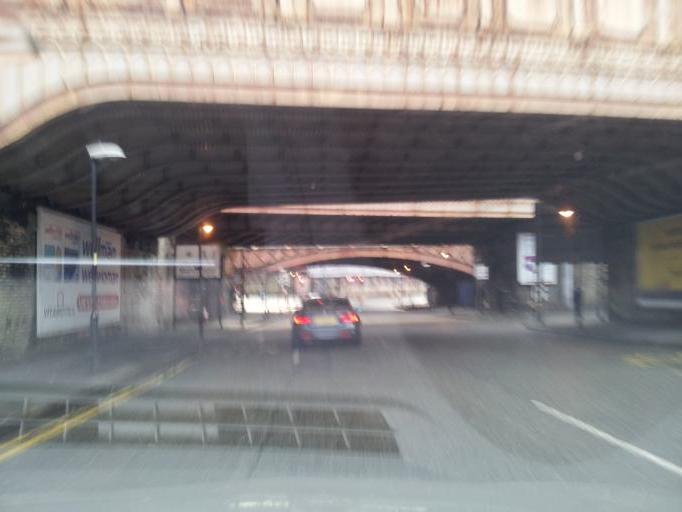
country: GB
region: England
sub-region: Manchester
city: Manchester
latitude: 53.4879
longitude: -2.2453
